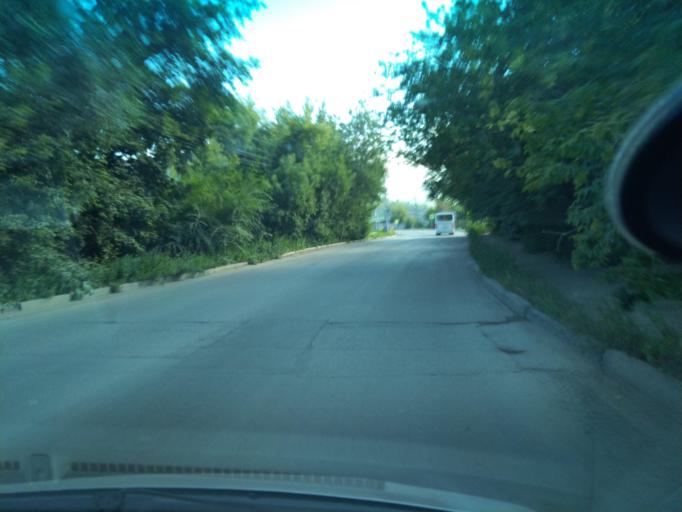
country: RU
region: Krasnoyarskiy
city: Krasnoyarsk
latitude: 55.9751
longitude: 92.9364
